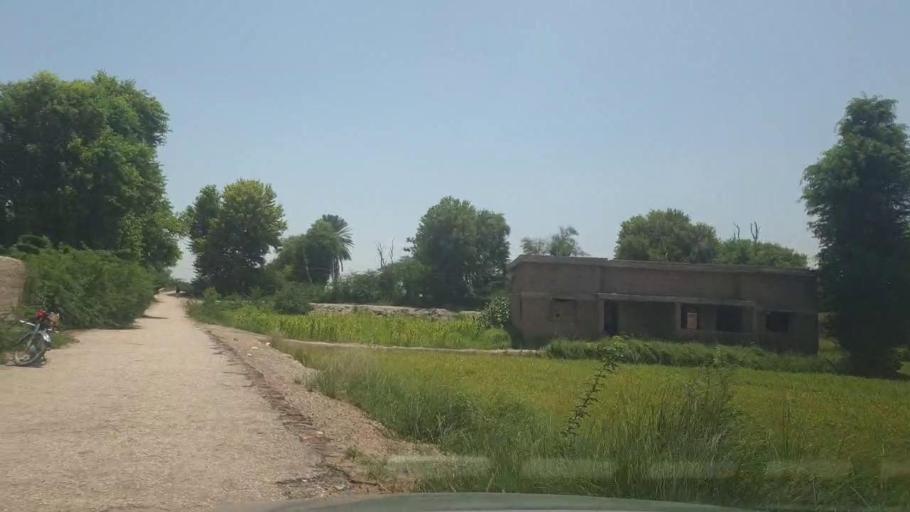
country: PK
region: Sindh
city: Kot Diji
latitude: 27.2648
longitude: 69.0176
